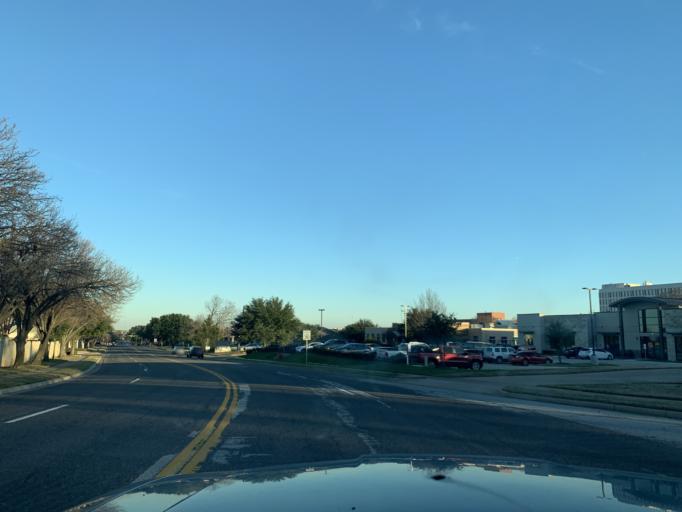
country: US
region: Texas
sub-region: Tarrant County
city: Bedford
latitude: 32.8413
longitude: -97.1369
